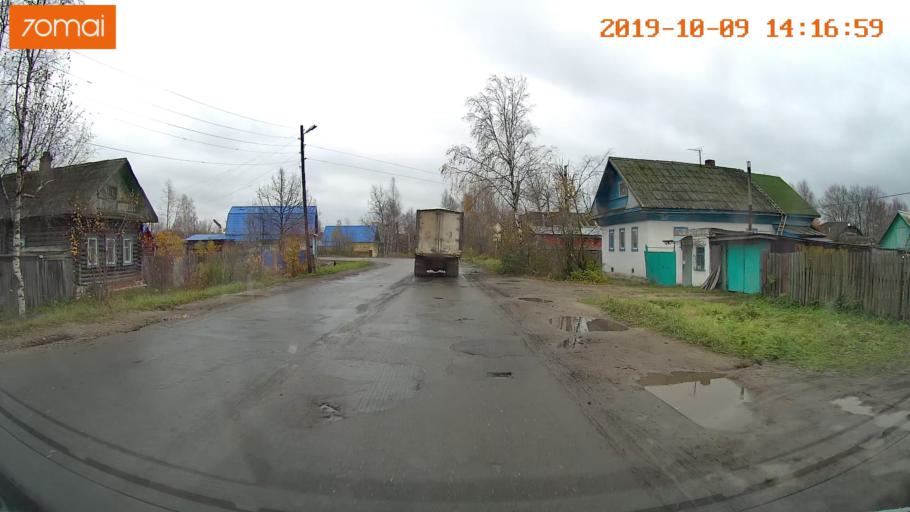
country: RU
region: Kostroma
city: Buy
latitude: 58.4811
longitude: 41.5223
